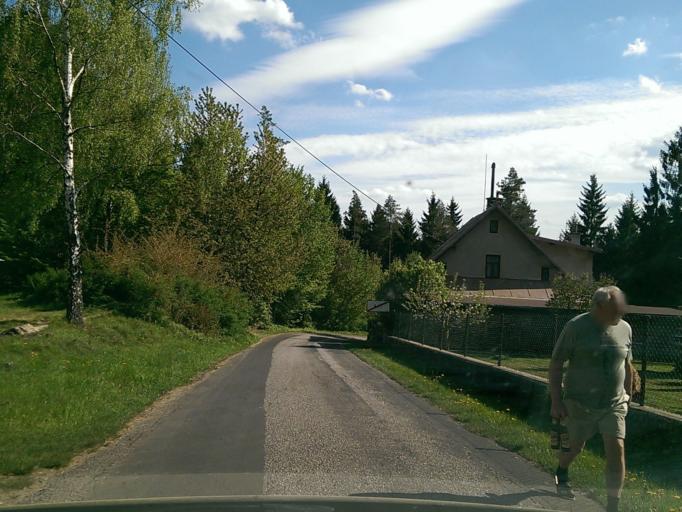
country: CZ
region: Liberecky
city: Mala Skala
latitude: 50.6564
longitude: 15.2253
